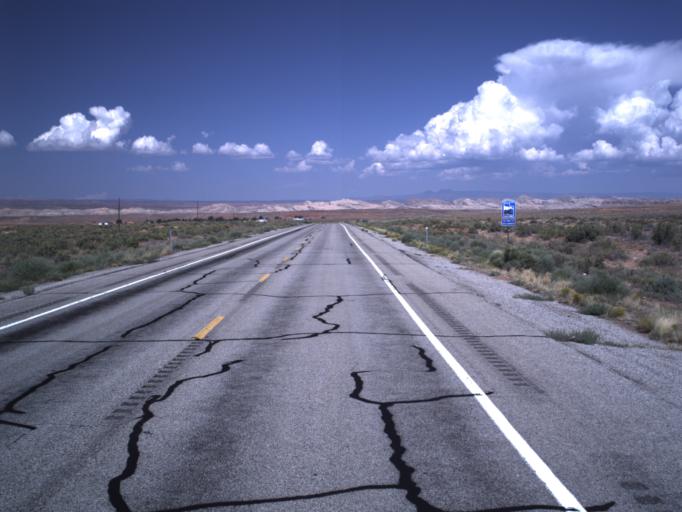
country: US
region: Utah
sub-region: San Juan County
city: Blanding
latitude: 37.1988
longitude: -109.6024
